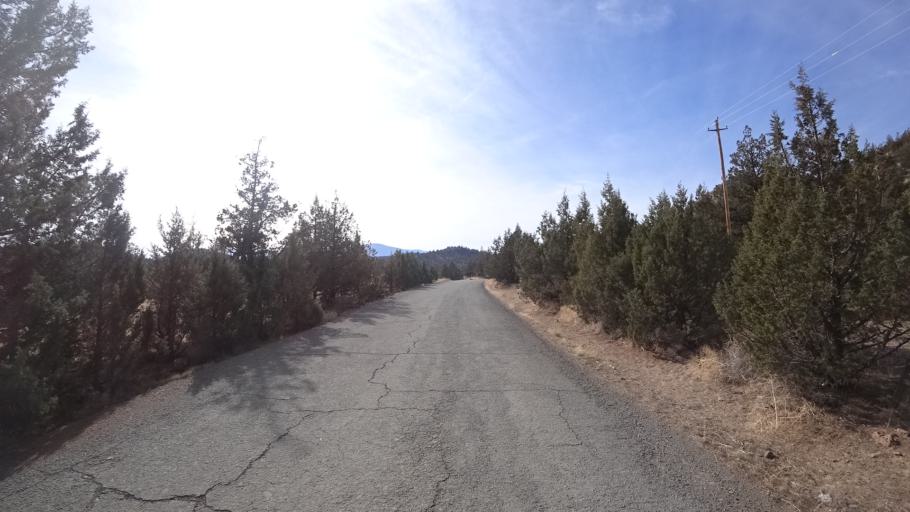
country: US
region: California
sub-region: Siskiyou County
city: Montague
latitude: 41.5867
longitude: -122.4433
